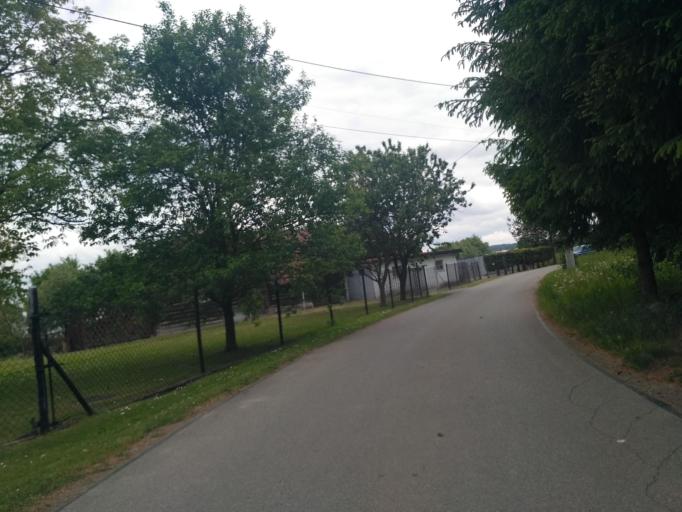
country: PL
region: Subcarpathian Voivodeship
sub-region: Powiat krosnienski
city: Jedlicze
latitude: 49.7032
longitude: 21.6759
